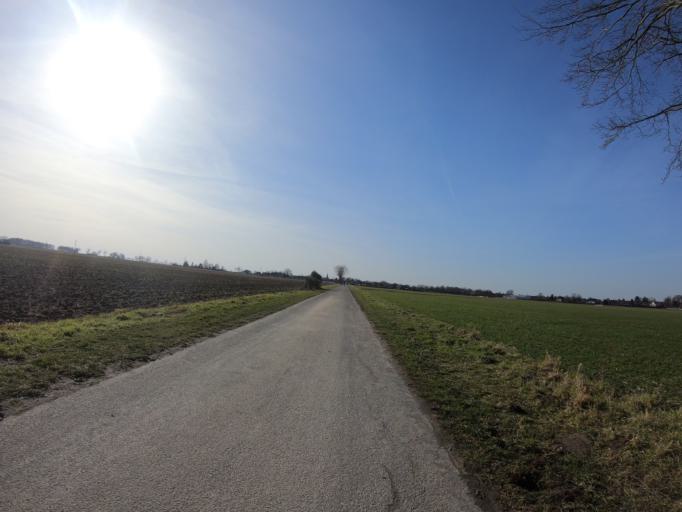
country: DE
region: Lower Saxony
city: Meine
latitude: 52.3891
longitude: 10.5548
